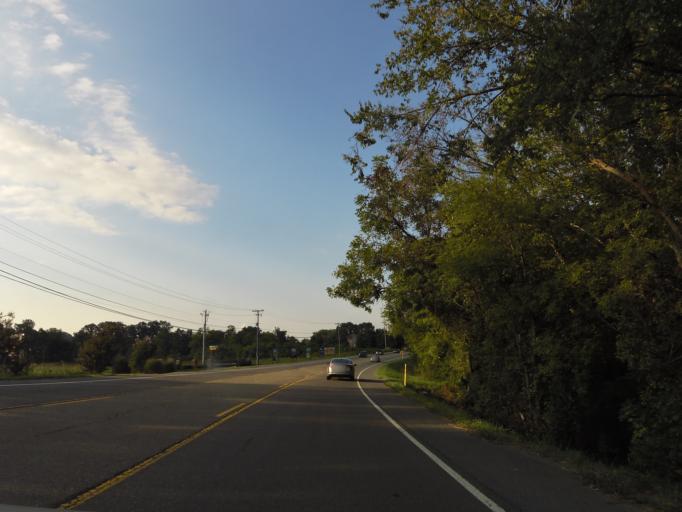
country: US
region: Tennessee
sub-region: Knox County
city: Knoxville
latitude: 35.9942
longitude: -83.8278
